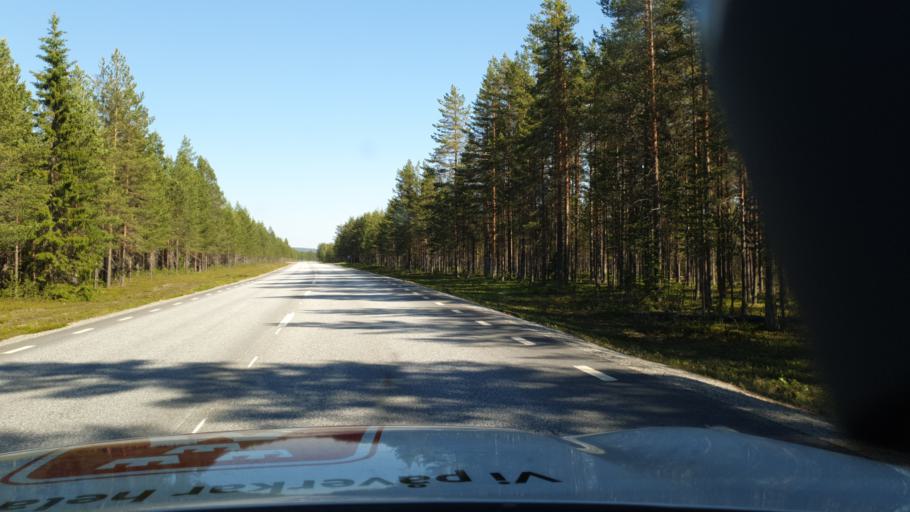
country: SE
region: Vaesterbotten
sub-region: Vindelns Kommun
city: Vindeln
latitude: 64.1628
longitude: 19.8157
